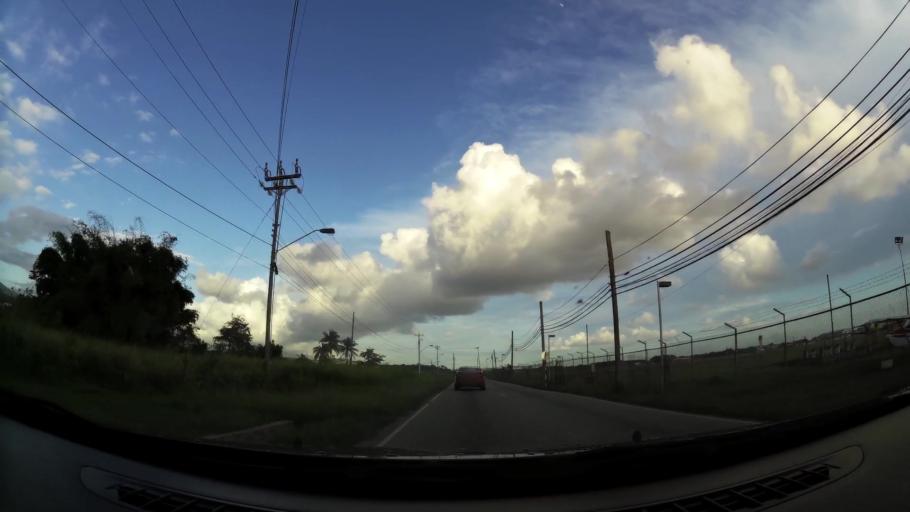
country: TT
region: Tunapuna/Piarco
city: Arouca
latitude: 10.5979
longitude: -61.3481
